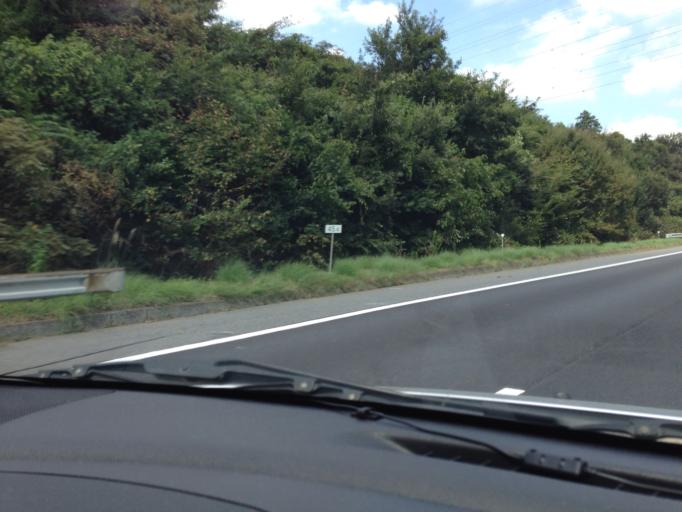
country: JP
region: Ibaraki
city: Naka
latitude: 36.1101
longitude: 140.1785
